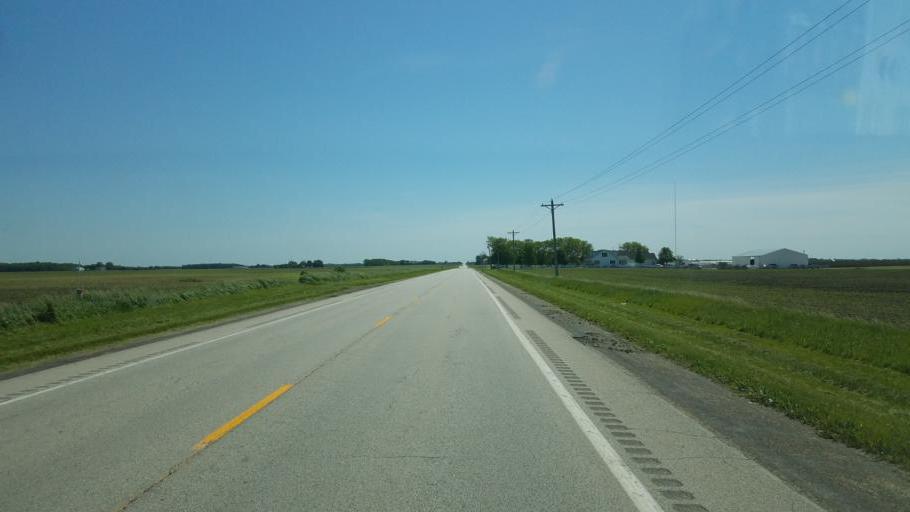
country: US
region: Illinois
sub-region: McLean County
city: Le Roy
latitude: 40.3118
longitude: -88.8125
